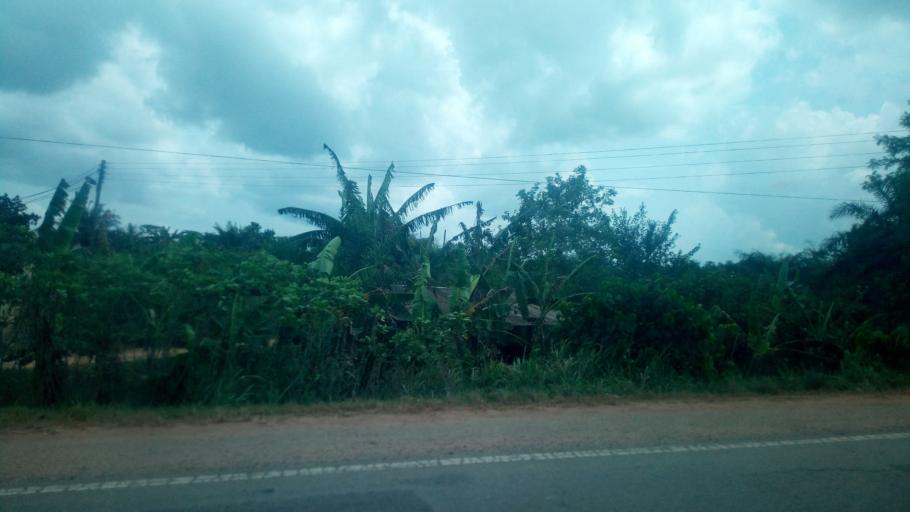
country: GH
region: Western
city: Takoradi
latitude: 4.8983
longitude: -1.9634
